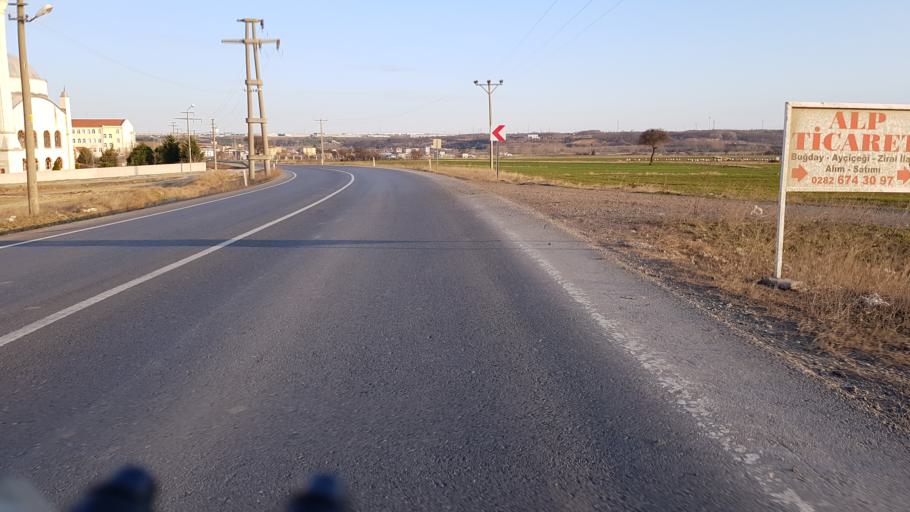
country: TR
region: Tekirdag
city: Velimese
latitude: 41.2526
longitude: 27.8657
